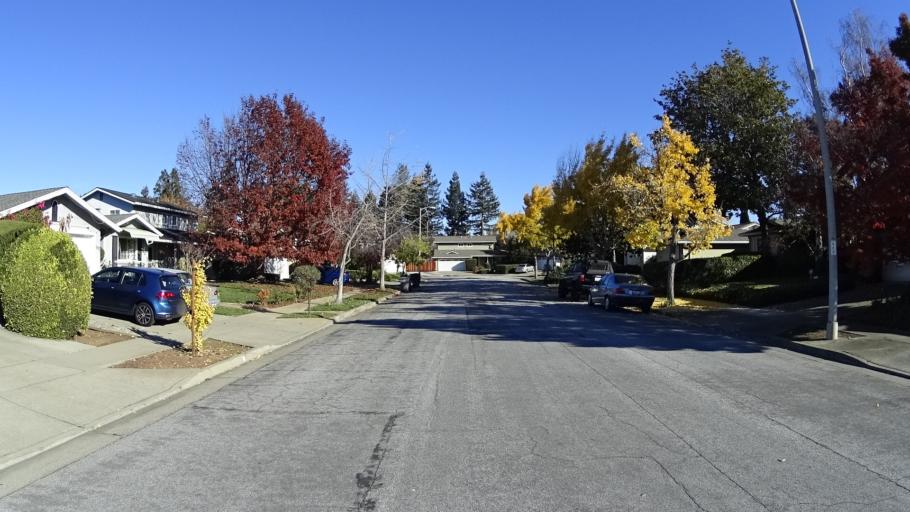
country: US
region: California
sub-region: Santa Clara County
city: Cupertino
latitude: 37.3420
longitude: -122.0292
